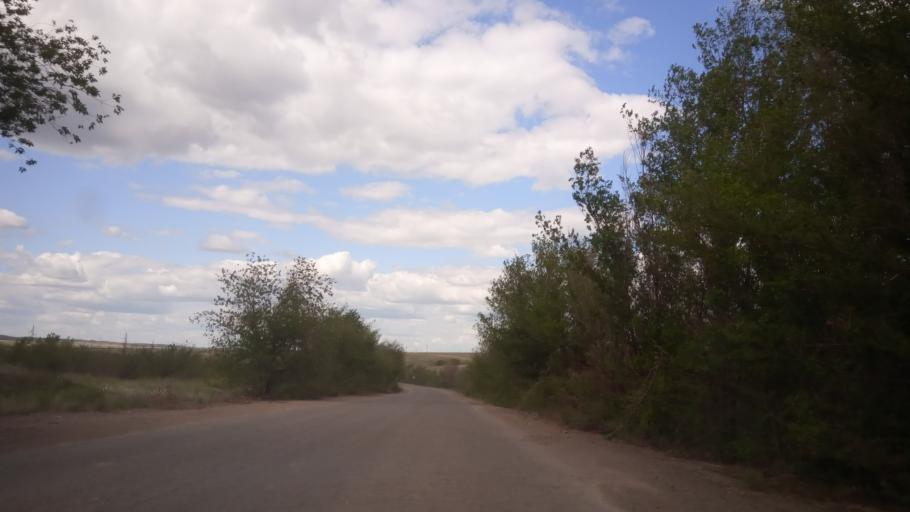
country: RU
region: Orenburg
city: Novotroitsk
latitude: 51.2507
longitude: 58.3648
